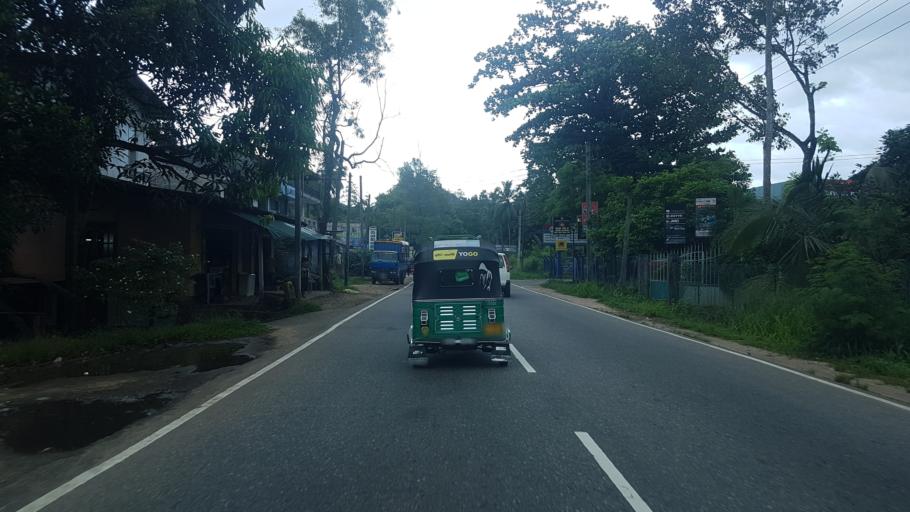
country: LK
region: Western
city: Hanwella Ihala
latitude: 7.0080
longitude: 80.2616
